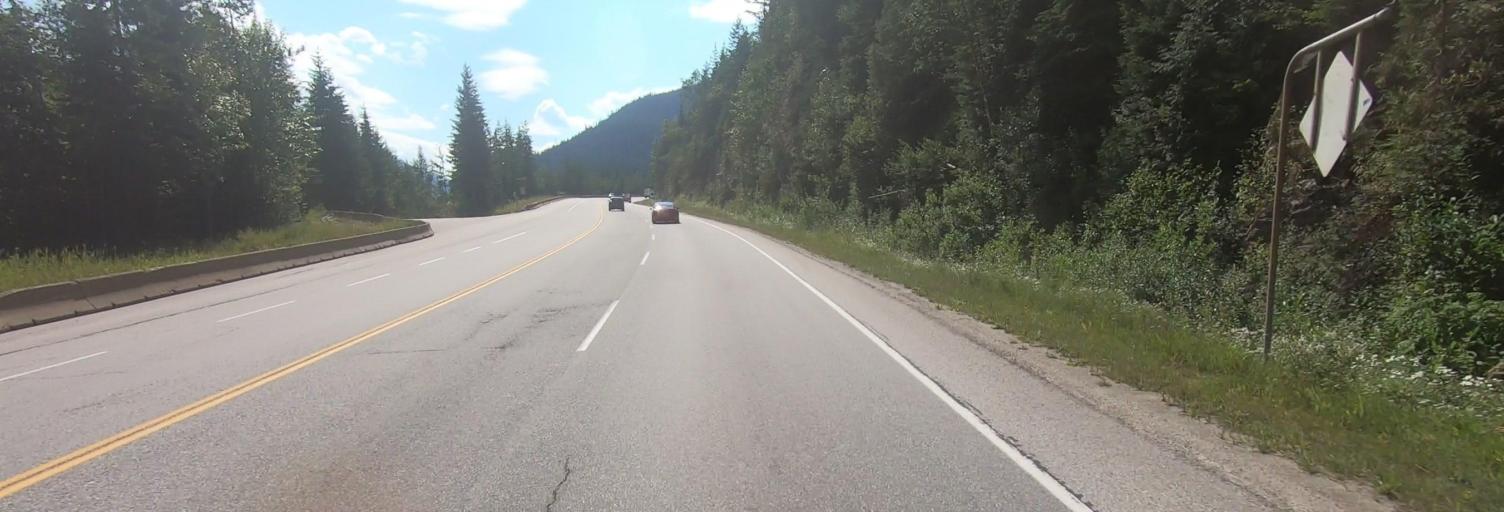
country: CA
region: British Columbia
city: Golden
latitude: 51.3556
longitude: -117.4380
